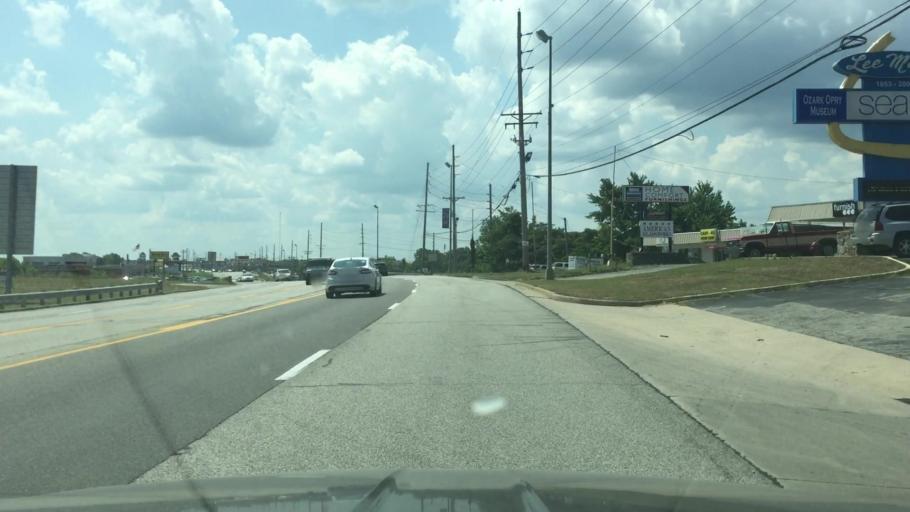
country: US
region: Missouri
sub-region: Miller County
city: Lake Ozark
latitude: 38.1671
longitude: -92.6110
